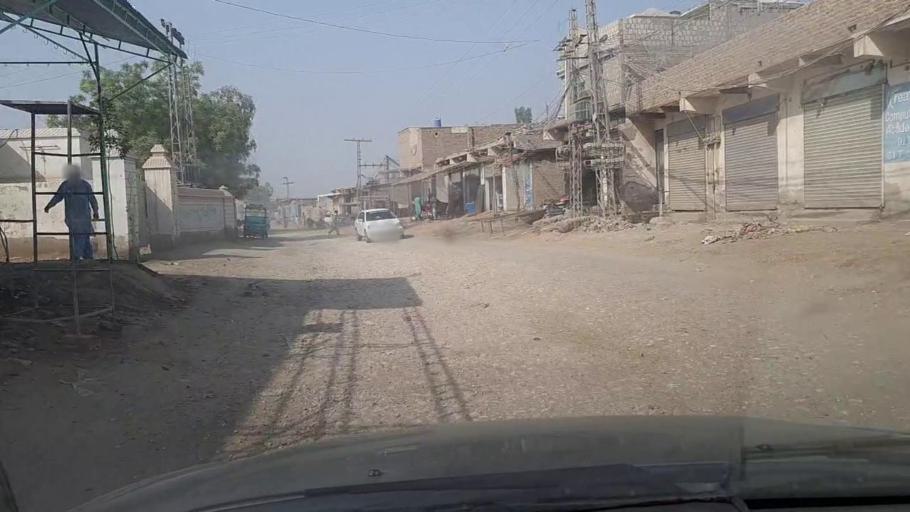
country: PK
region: Sindh
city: Mirpur Mathelo
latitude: 28.0172
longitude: 69.5496
